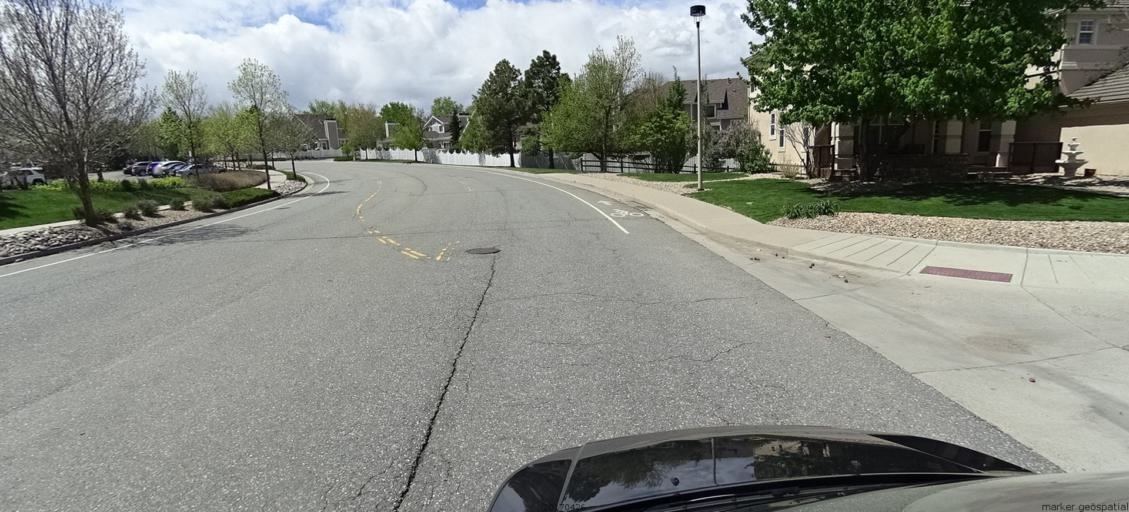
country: US
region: Colorado
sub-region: Douglas County
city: Carriage Club
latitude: 39.5382
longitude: -104.8887
